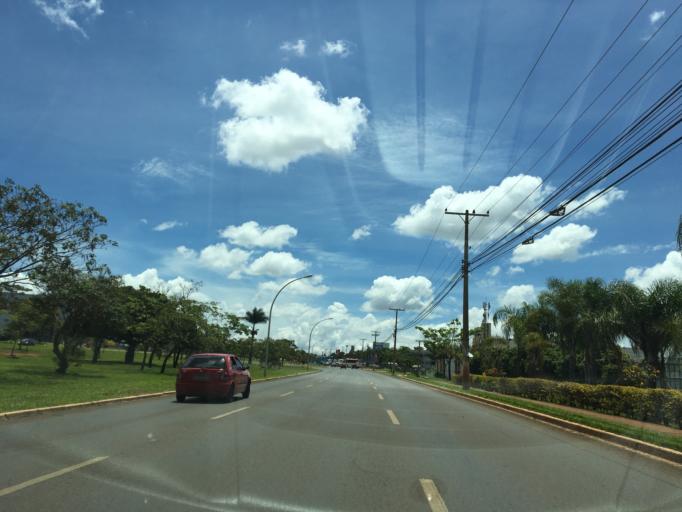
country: BR
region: Federal District
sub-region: Brasilia
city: Brasilia
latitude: -15.7326
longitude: -47.8961
